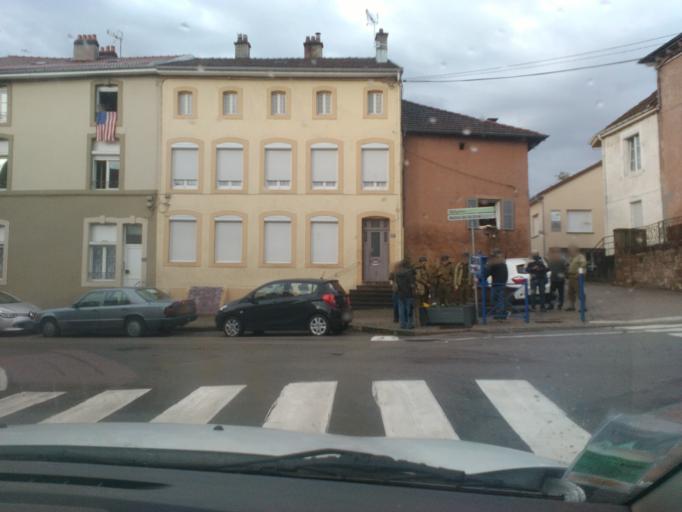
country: FR
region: Lorraine
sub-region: Departement des Vosges
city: Bruyeres
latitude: 48.2117
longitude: 6.7200
